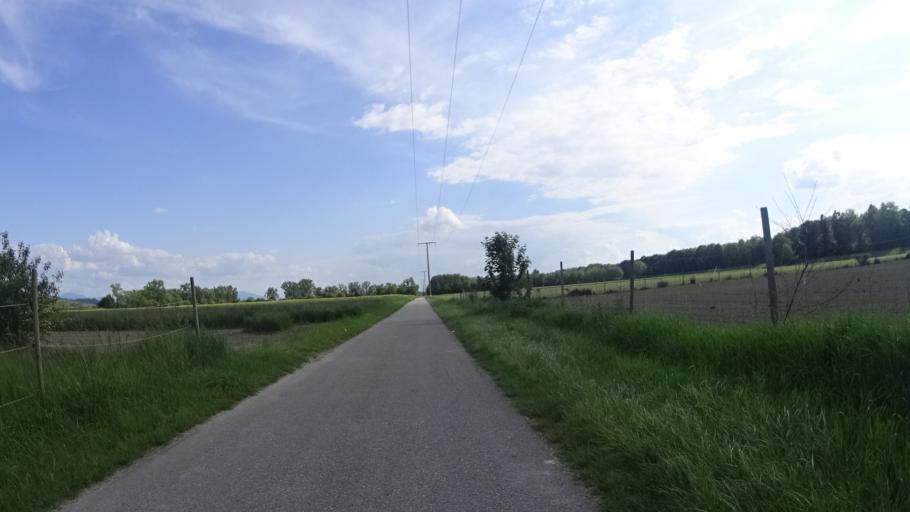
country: DE
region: Baden-Wuerttemberg
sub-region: Freiburg Region
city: Breisach am Rhein
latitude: 48.0772
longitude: 7.5917
